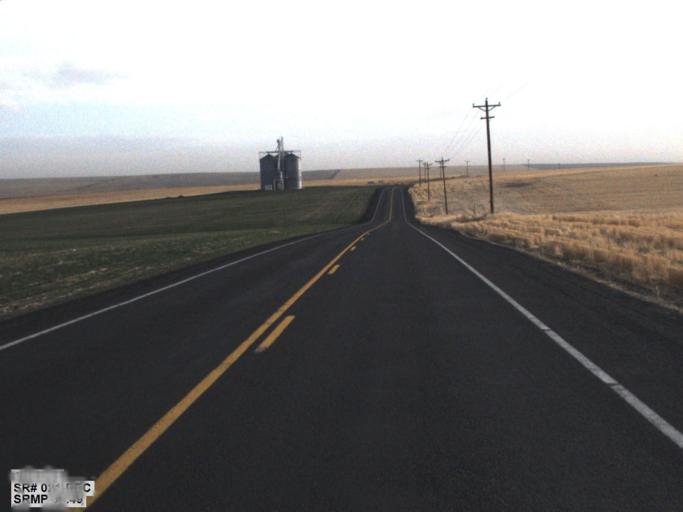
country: US
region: Washington
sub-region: Adams County
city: Ritzville
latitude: 47.1068
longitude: -118.6653
